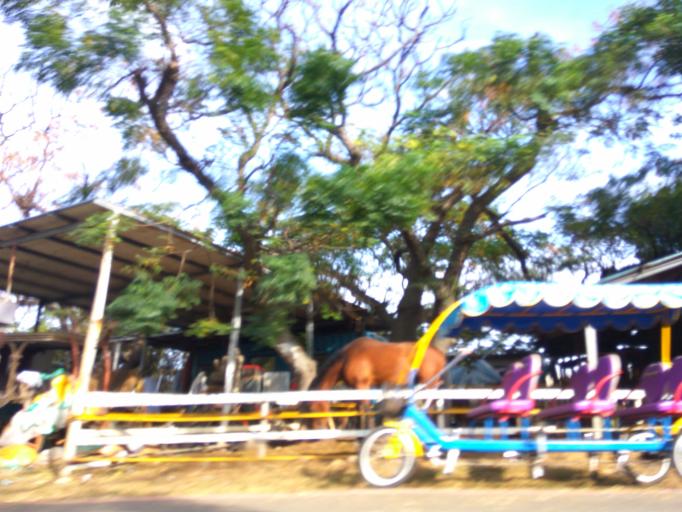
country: TW
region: Taiwan
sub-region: Hsinchu
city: Zhubei
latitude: 24.9849
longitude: 121.0181
